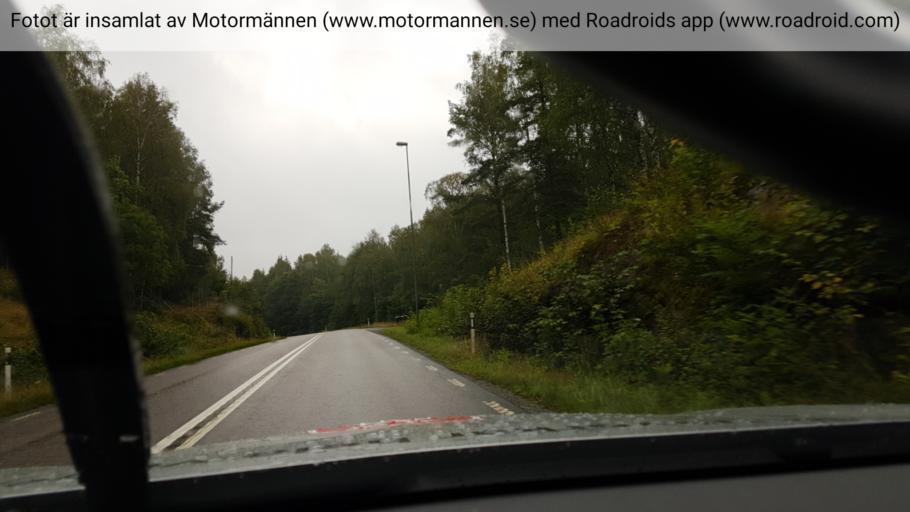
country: SE
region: Vaestra Goetaland
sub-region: Bengtsfors Kommun
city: Billingsfors
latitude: 58.9915
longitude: 12.2658
